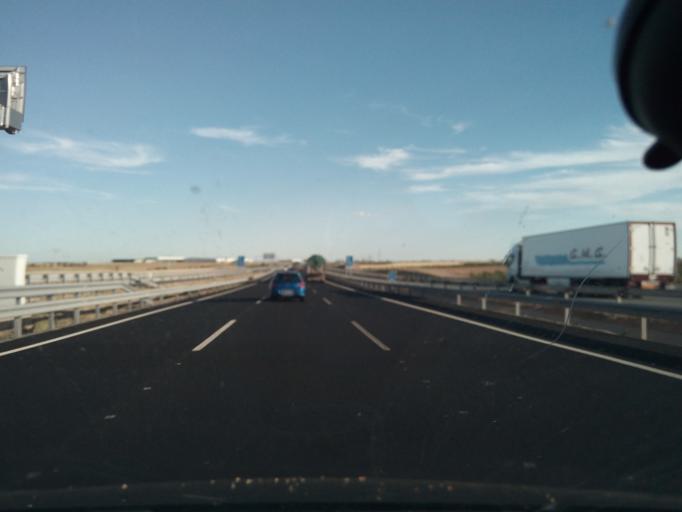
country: ES
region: Castille-La Mancha
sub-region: Province of Toledo
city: Dosbarrios
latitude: 39.9070
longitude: -3.4750
